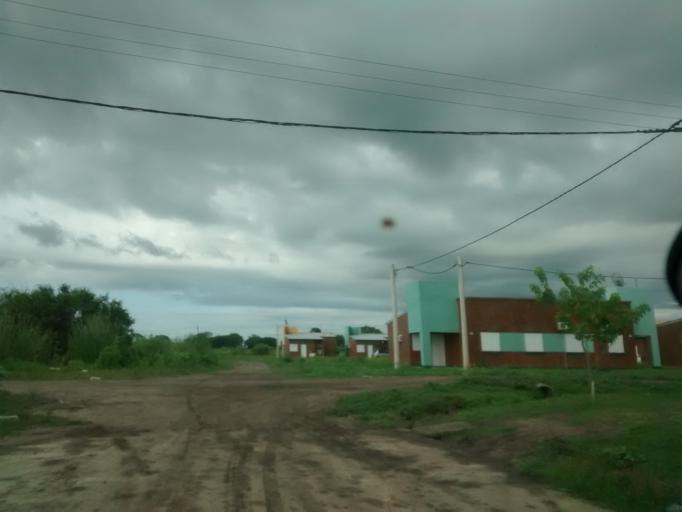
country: AR
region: Chaco
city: Puerto Tirol
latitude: -27.3807
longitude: -59.0922
